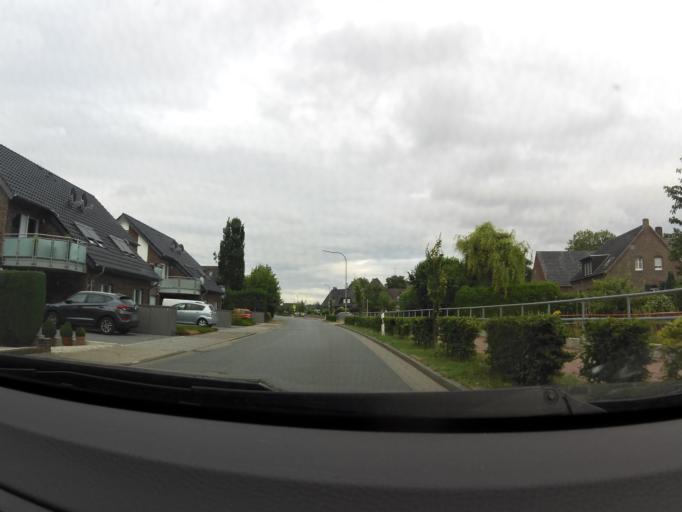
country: DE
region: North Rhine-Westphalia
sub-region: Regierungsbezirk Dusseldorf
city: Kevelaer
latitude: 51.5375
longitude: 6.2407
